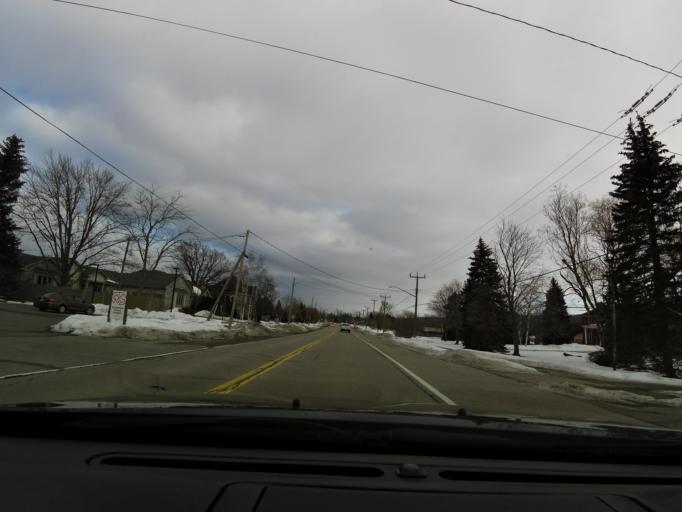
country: CA
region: Ontario
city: Hamilton
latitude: 43.2074
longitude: -79.6486
